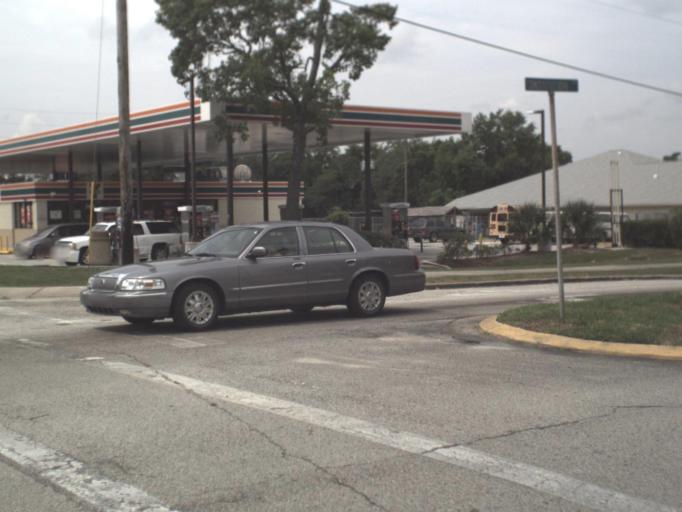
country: US
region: Florida
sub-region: Clay County
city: Bellair-Meadowbrook Terrace
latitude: 30.1588
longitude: -81.7474
